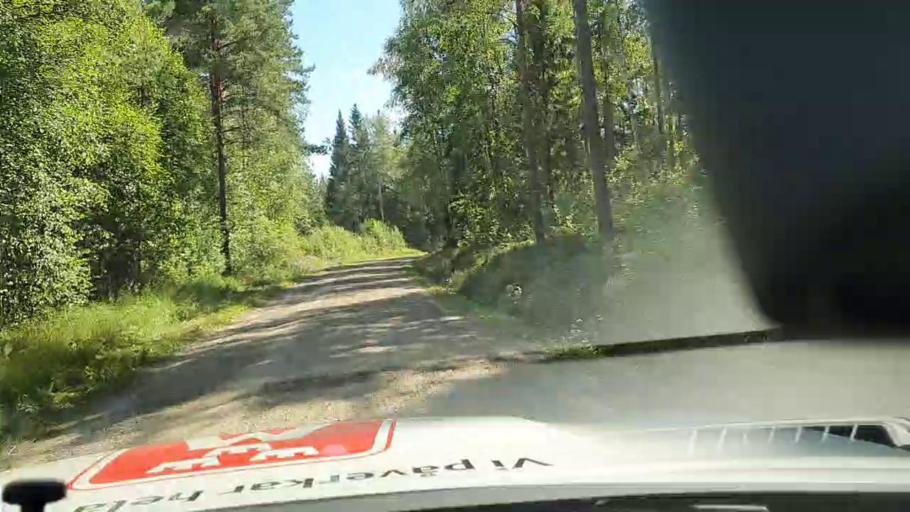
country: SE
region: Soedermanland
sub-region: Strangnas Kommun
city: Akers Styckebruk
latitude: 59.2082
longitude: 16.9177
